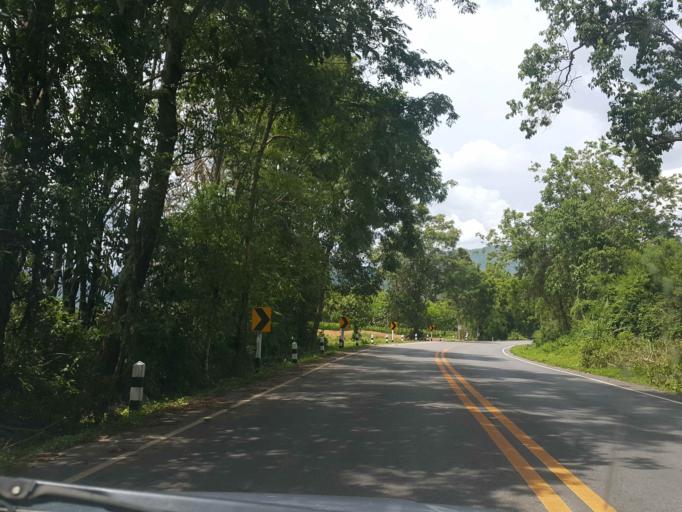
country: TH
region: Nan
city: Ban Luang
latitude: 18.8635
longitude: 100.4642
